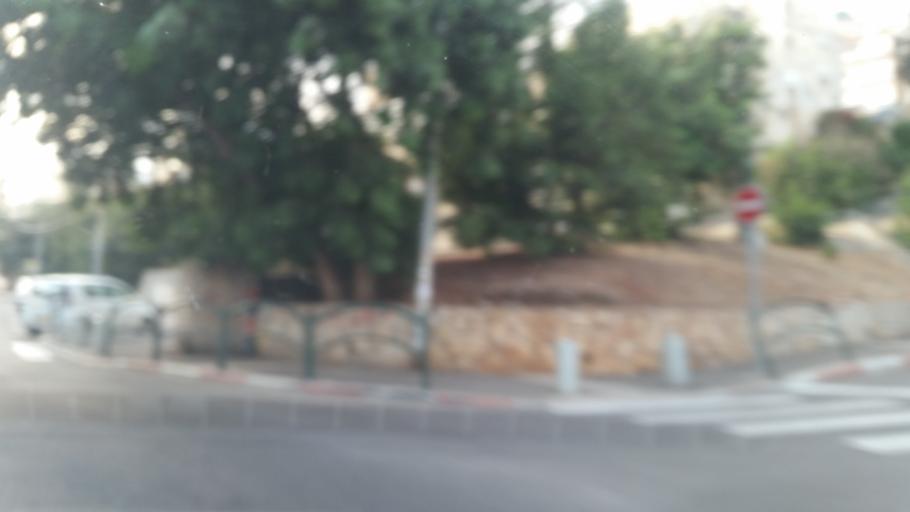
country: IL
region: Haifa
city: Haifa
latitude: 32.7999
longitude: 35.0120
